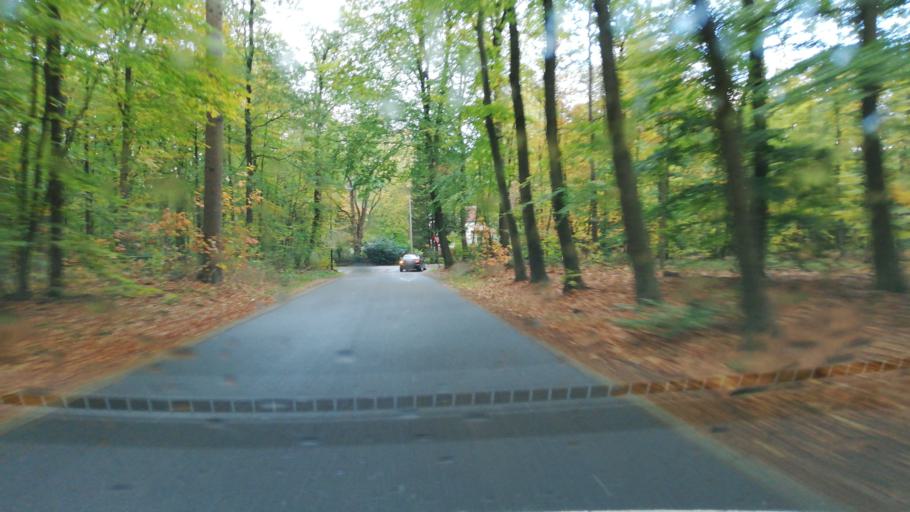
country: NL
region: Gelderland
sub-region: Gemeente Apeldoorn
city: Beekbergen
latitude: 52.1503
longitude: 5.9750
